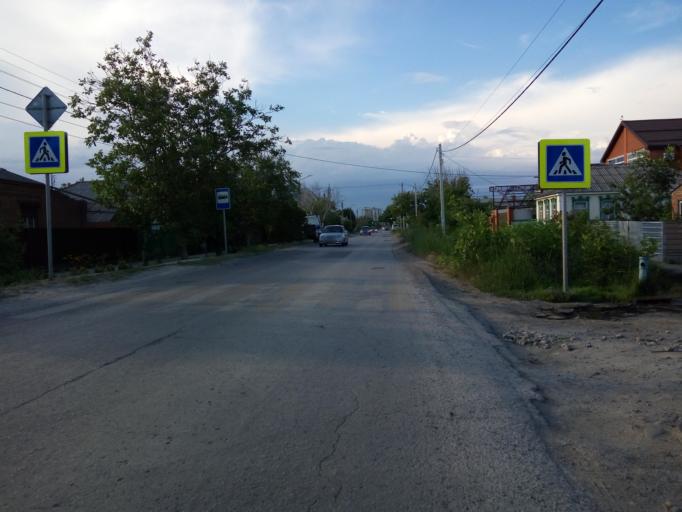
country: RU
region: Rostov
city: Bataysk
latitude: 47.1160
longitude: 39.7396
